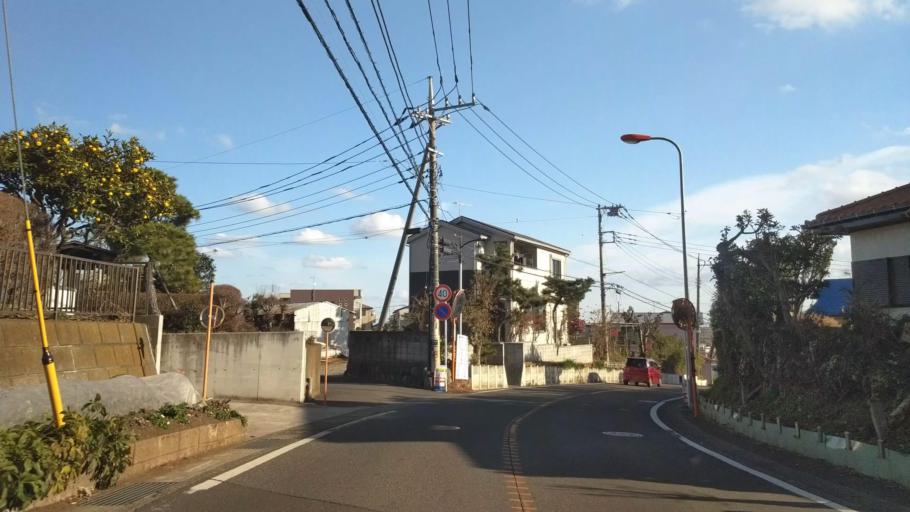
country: JP
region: Kanagawa
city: Isehara
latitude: 35.3775
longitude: 139.2814
